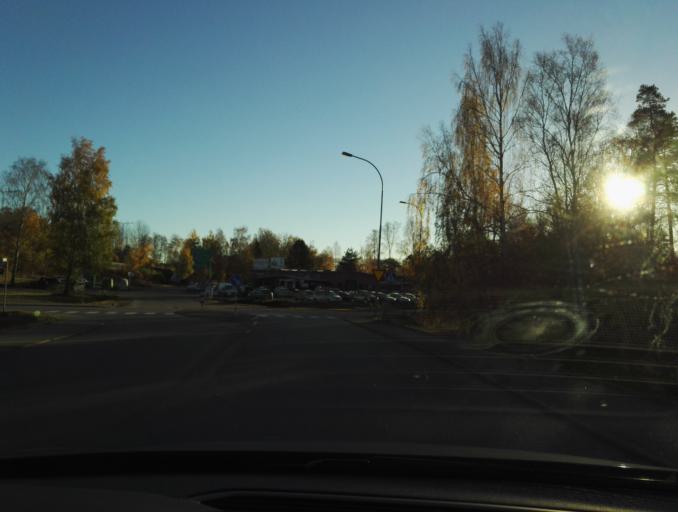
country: SE
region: Kronoberg
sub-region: Vaxjo Kommun
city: Vaexjoe
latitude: 56.8943
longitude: 14.7371
